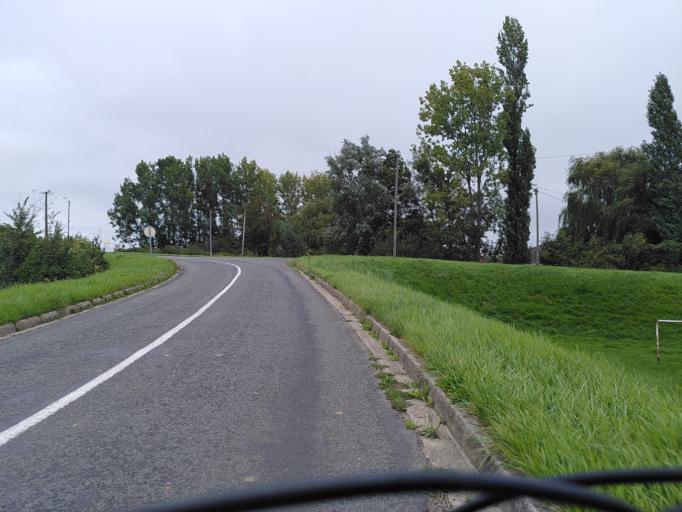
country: FR
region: Nord-Pas-de-Calais
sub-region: Departement du Pas-de-Calais
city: Isbergues
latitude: 50.6338
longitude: 2.4378
